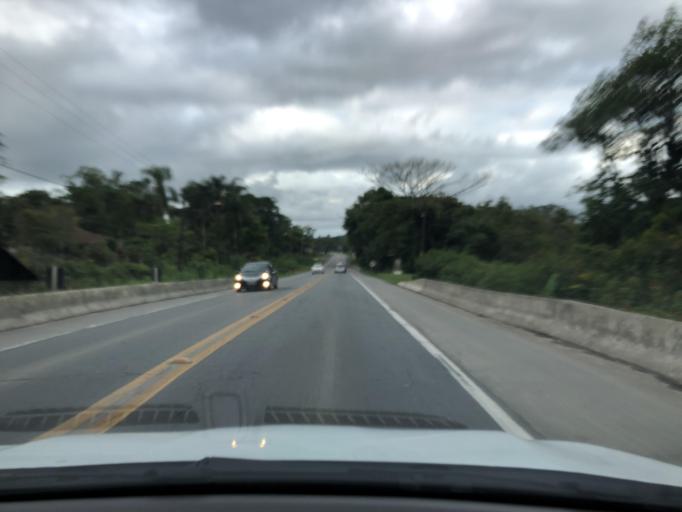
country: BR
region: Santa Catarina
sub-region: Sao Francisco Do Sul
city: Sao Francisco do Sul
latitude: -26.3071
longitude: -48.6420
